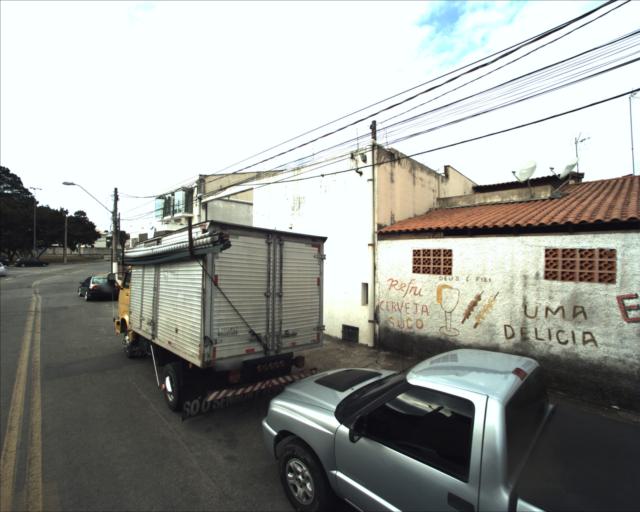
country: BR
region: Sao Paulo
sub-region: Sorocaba
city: Sorocaba
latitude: -23.5160
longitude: -47.4433
